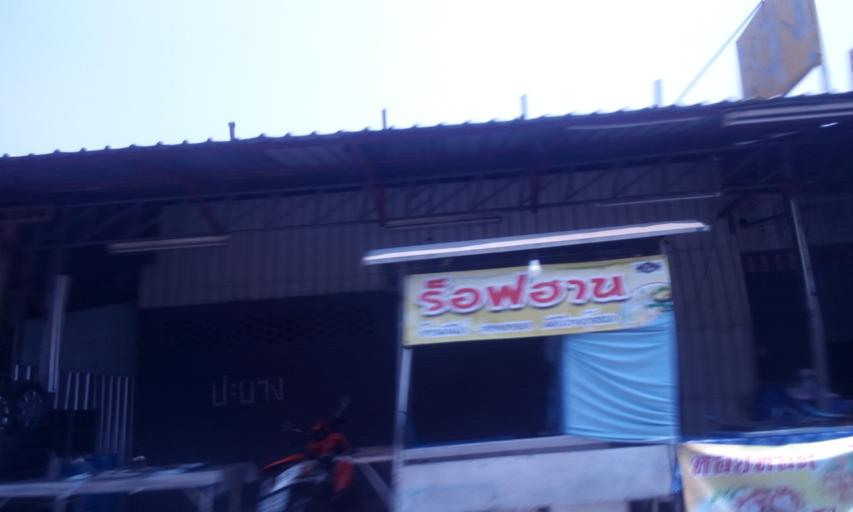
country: TH
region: Chachoengsao
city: Bang Nam Priao
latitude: 13.9654
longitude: 100.9656
